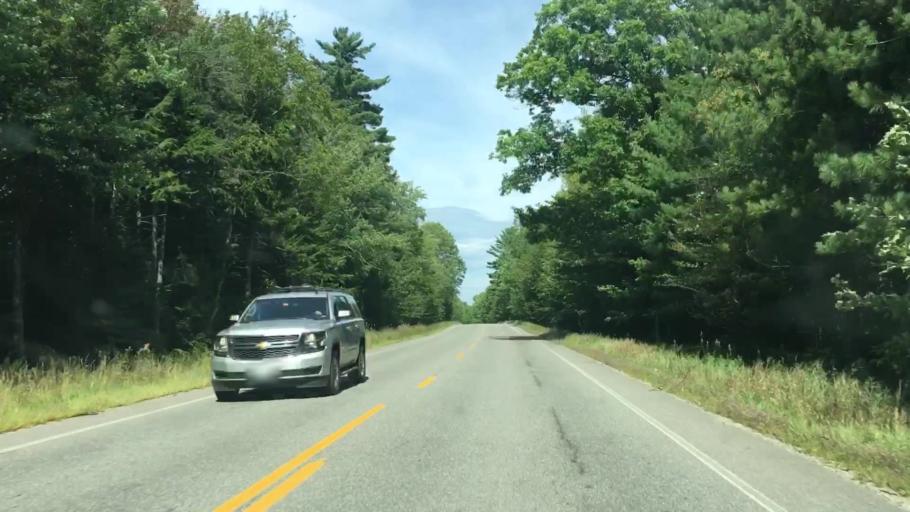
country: US
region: Maine
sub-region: Penobscot County
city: Lincoln
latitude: 45.3758
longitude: -68.5518
